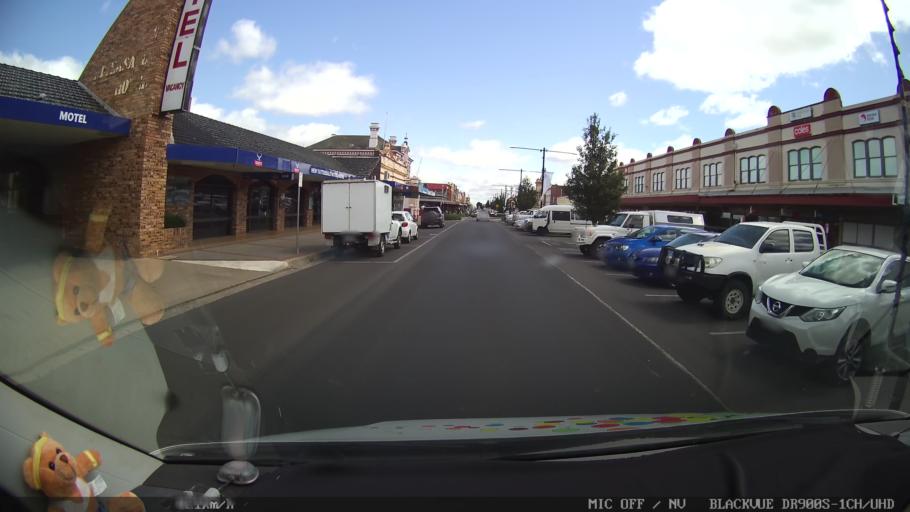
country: AU
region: New South Wales
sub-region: Glen Innes Severn
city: Glen Innes
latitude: -29.7399
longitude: 151.7352
